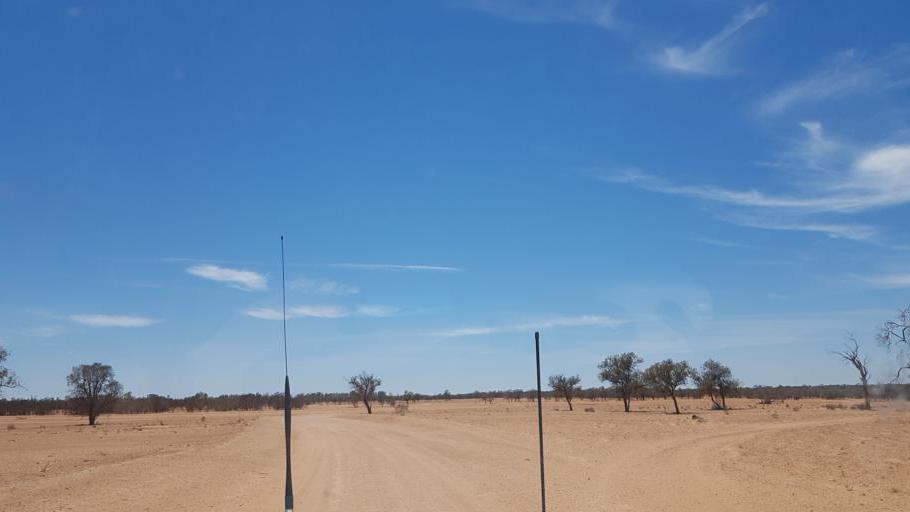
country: AU
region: New South Wales
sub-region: Wentworth
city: Dareton
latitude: -33.3465
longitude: 141.4564
